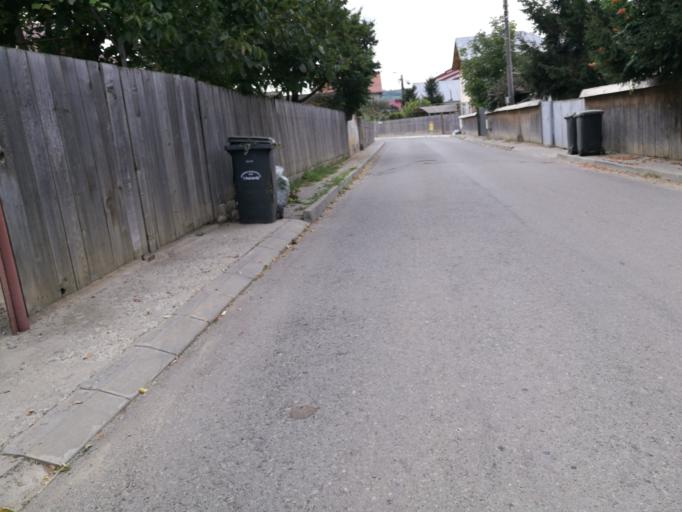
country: RO
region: Iasi
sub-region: Comuna Miroslava
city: Miroslava
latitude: 47.1748
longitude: 27.5285
